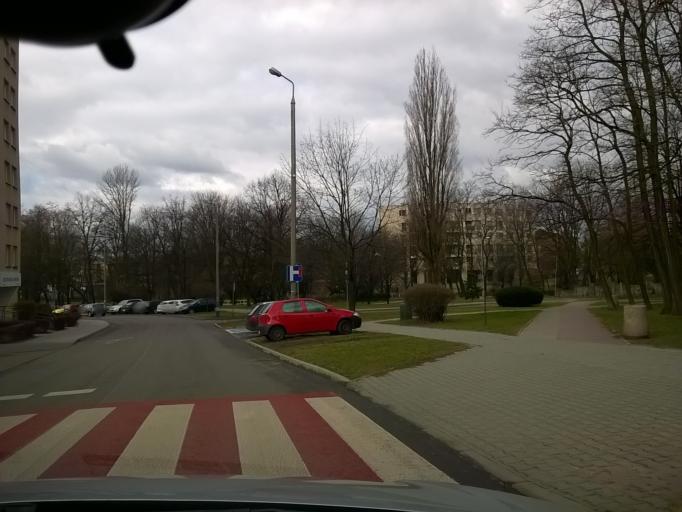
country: PL
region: Silesian Voivodeship
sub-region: Chorzow
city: Chorzow
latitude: 50.2863
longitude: 18.9534
